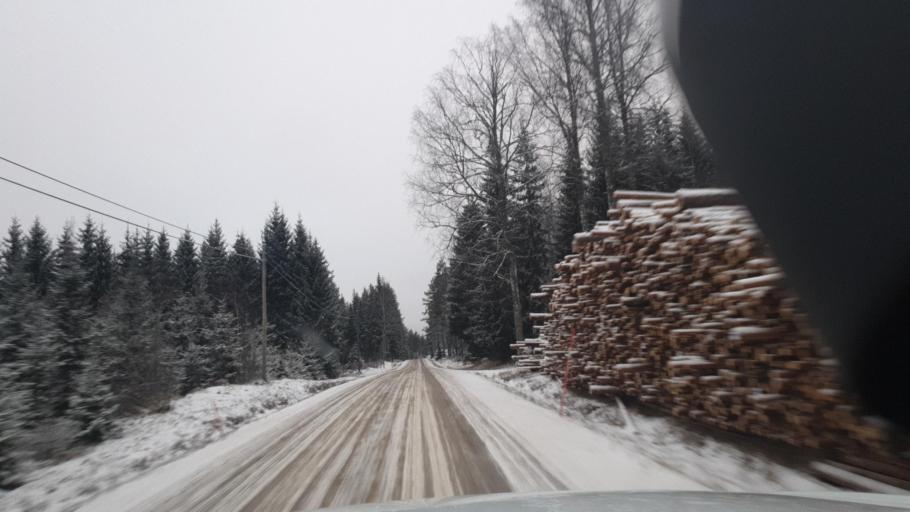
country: SE
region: Vaermland
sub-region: Eda Kommun
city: Charlottenberg
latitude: 59.9751
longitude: 12.4938
